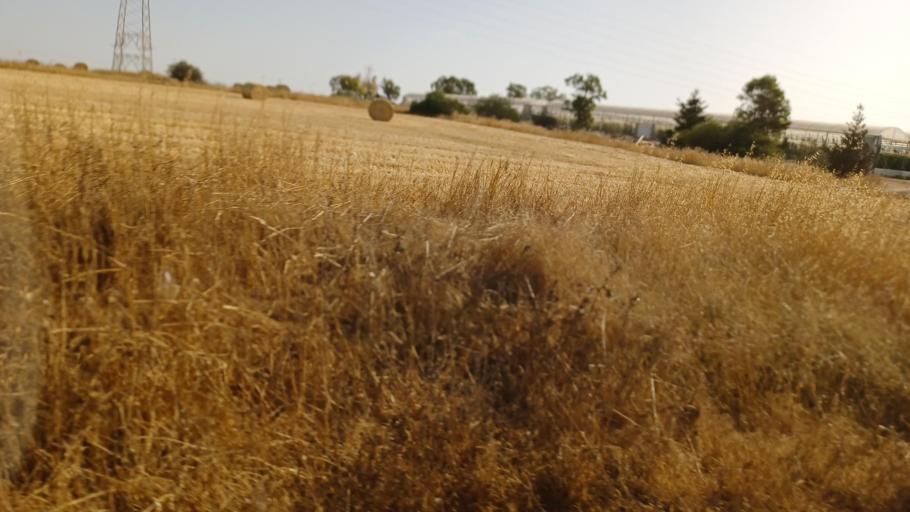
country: CY
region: Ammochostos
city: Liopetri
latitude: 35.0012
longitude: 33.9293
